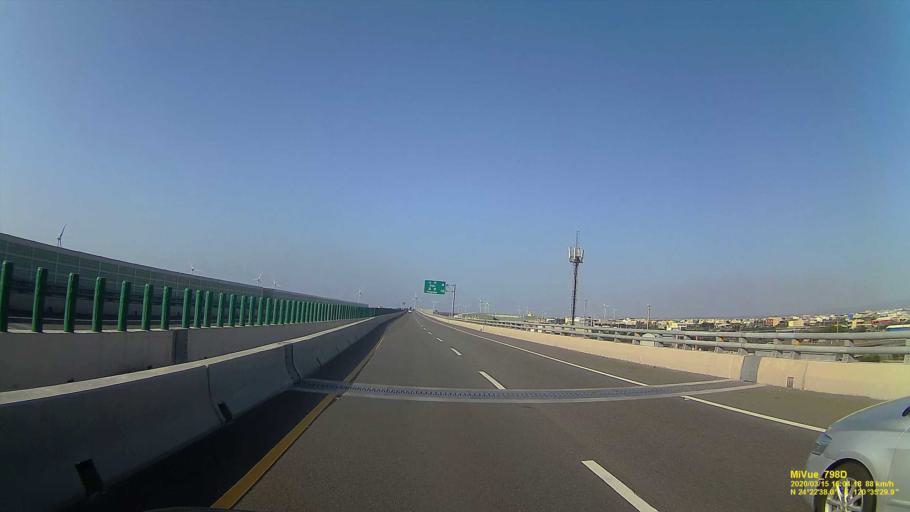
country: TW
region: Taiwan
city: Fengyuan
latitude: 24.3774
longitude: 120.5919
